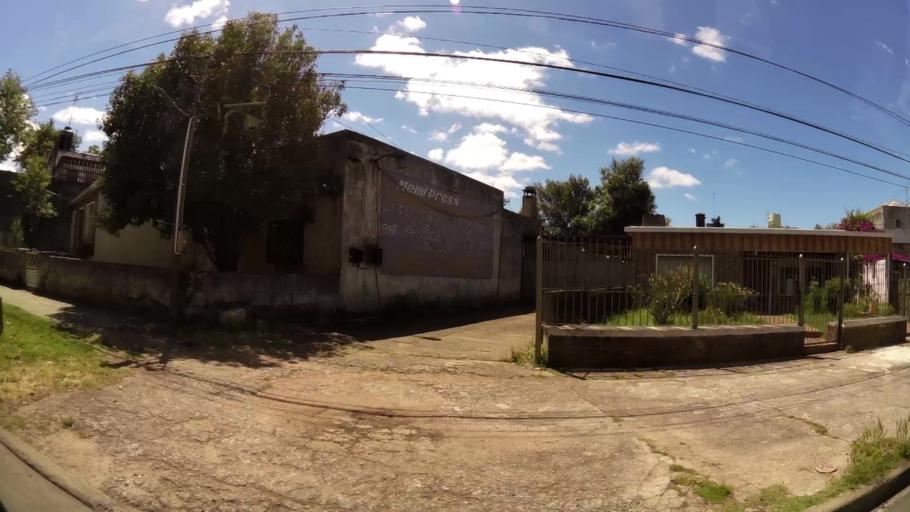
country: UY
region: Montevideo
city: Montevideo
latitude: -34.8592
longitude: -56.1349
